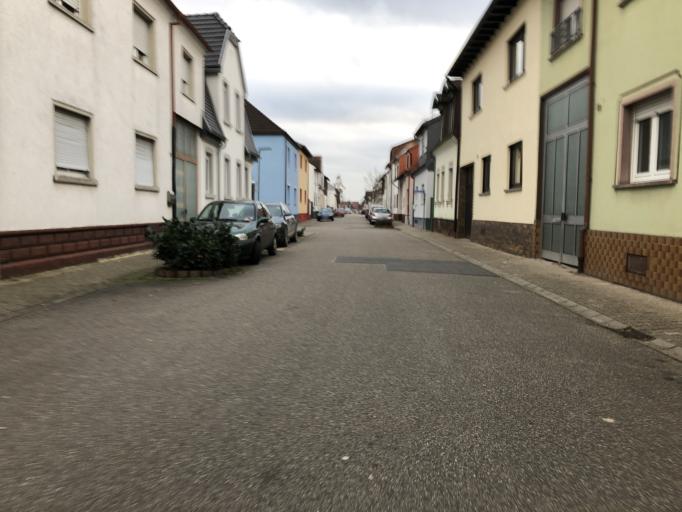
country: DE
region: Baden-Wuerttemberg
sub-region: Karlsruhe Region
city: Altlussheim
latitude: 49.2977
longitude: 8.4996
